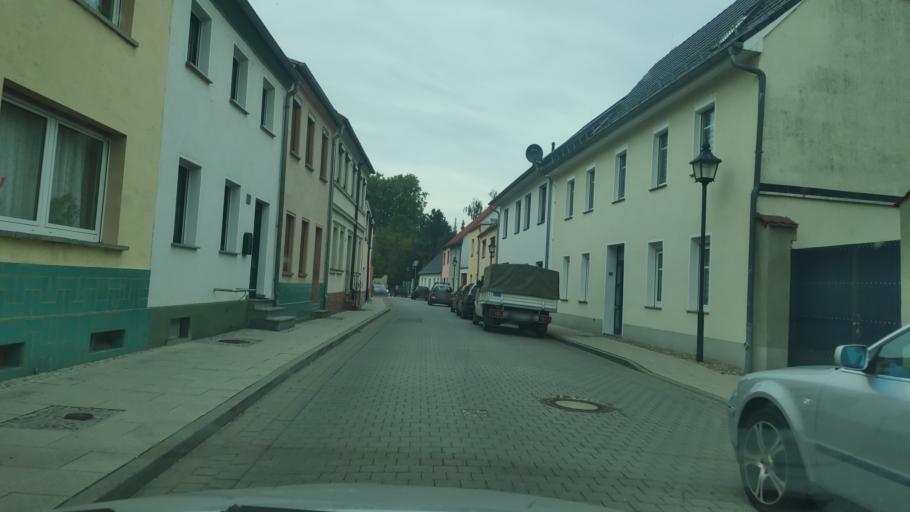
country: DE
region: Saxony-Anhalt
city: Barby
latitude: 51.9682
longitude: 11.8872
